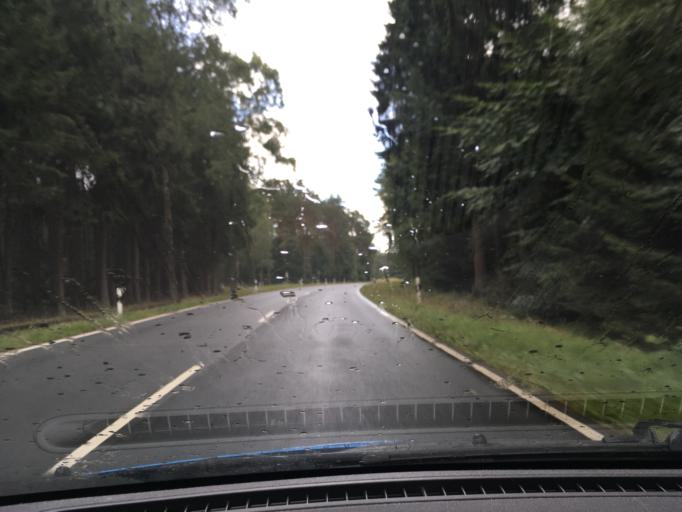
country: DE
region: Lower Saxony
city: Wietzendorf
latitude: 52.9730
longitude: 9.9514
